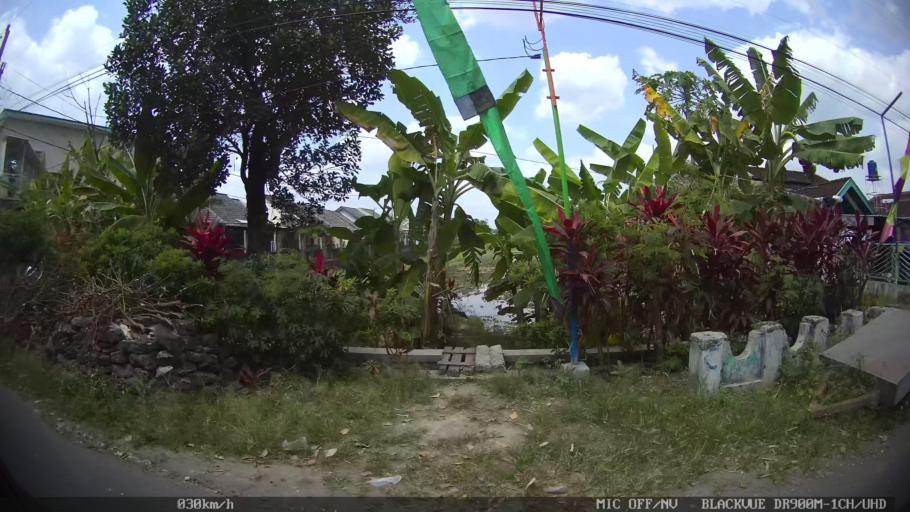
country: ID
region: Daerah Istimewa Yogyakarta
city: Kasihan
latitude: -7.8171
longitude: 110.3403
